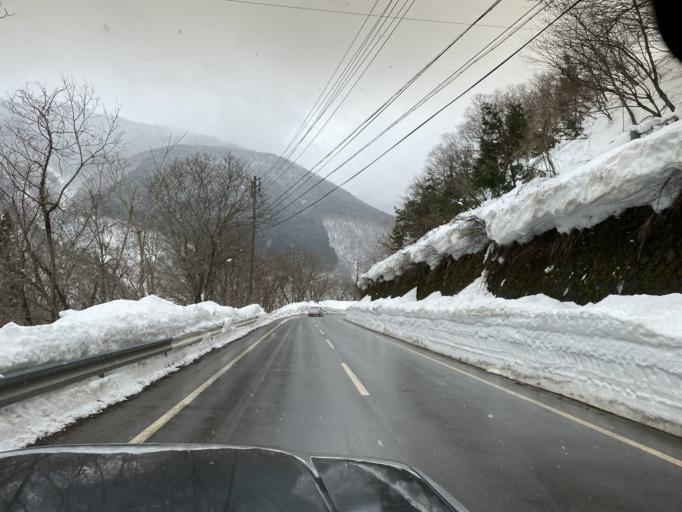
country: JP
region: Toyama
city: Fukumitsu
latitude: 36.2131
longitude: 136.8896
